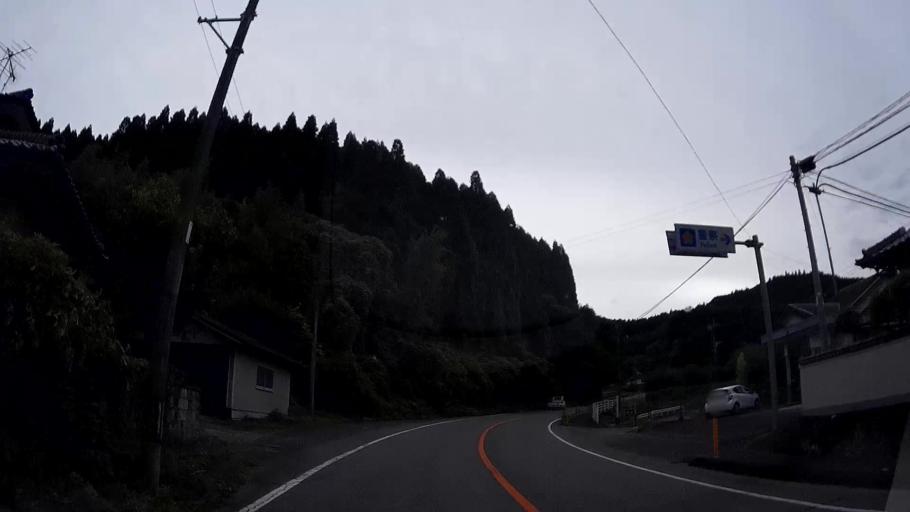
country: JP
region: Kumamoto
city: Kikuchi
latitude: 33.0159
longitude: 130.8795
